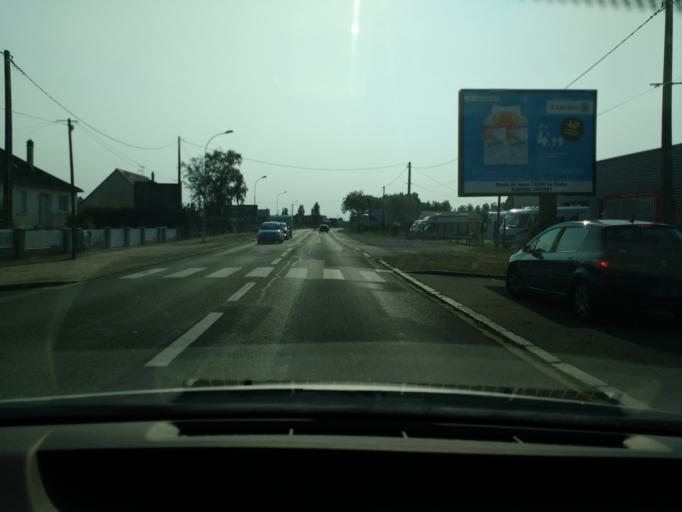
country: FR
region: Pays de la Loire
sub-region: Departement de la Sarthe
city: La Fleche
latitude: 47.6967
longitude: -0.0928
